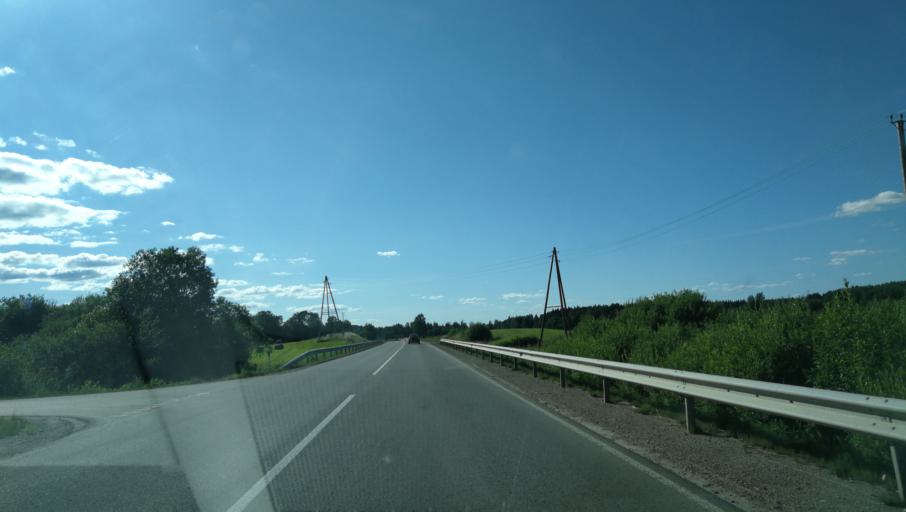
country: LV
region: Vecpiebalga
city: Vecpiebalga
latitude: 57.0740
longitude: 25.7792
